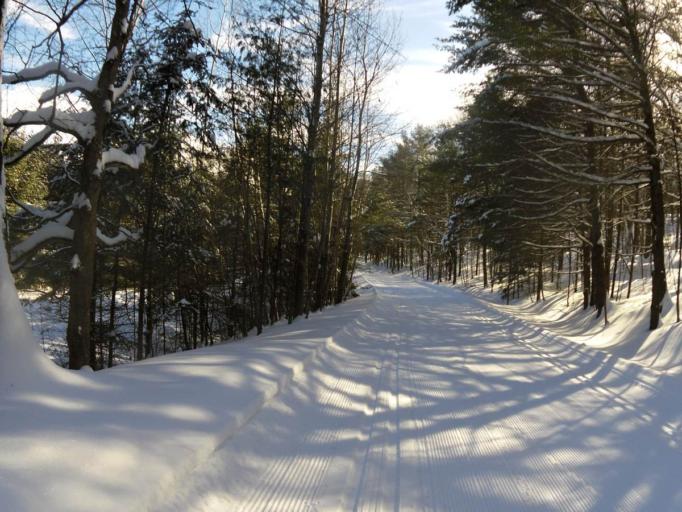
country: CA
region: Quebec
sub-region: Outaouais
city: Wakefield
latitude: 45.6038
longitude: -76.0116
